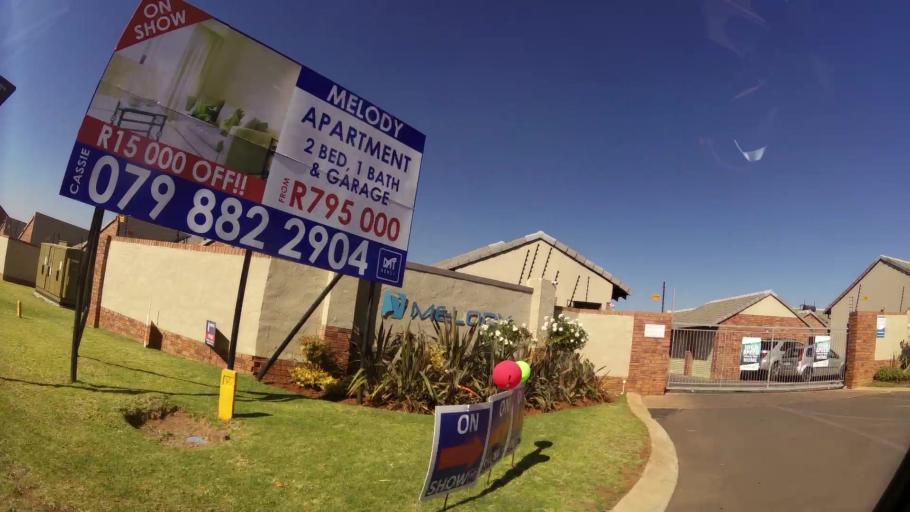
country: ZA
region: Gauteng
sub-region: City of Johannesburg Metropolitan Municipality
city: Midrand
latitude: -25.9484
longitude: 28.1037
